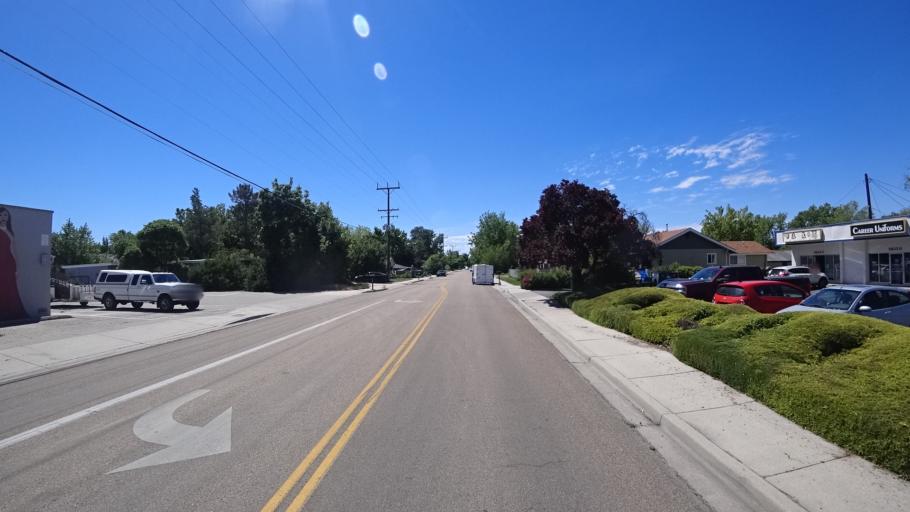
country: US
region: Idaho
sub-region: Ada County
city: Garden City
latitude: 43.5896
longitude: -116.2287
